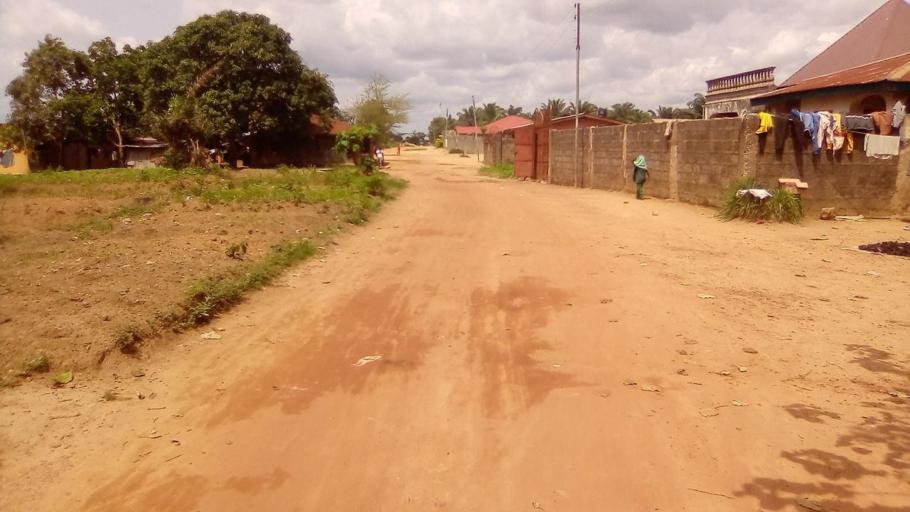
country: SL
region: Southern Province
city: Bo
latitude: 7.9670
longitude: -11.7245
